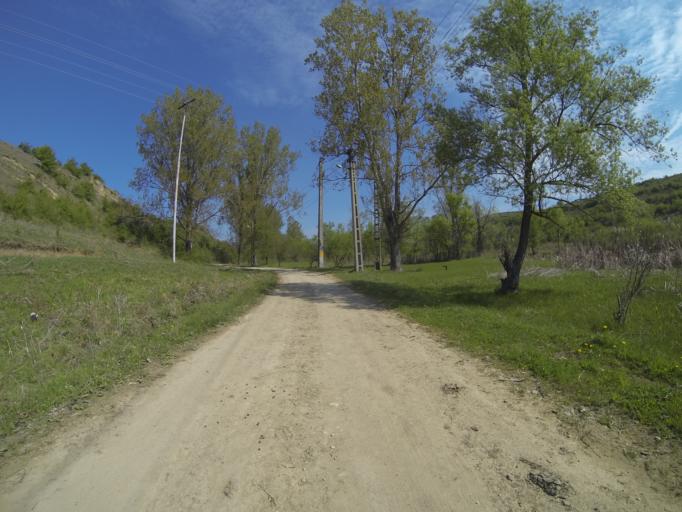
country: RO
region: Dolj
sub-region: Comuna Bradesti
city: Bradesti
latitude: 44.5309
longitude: 23.6259
